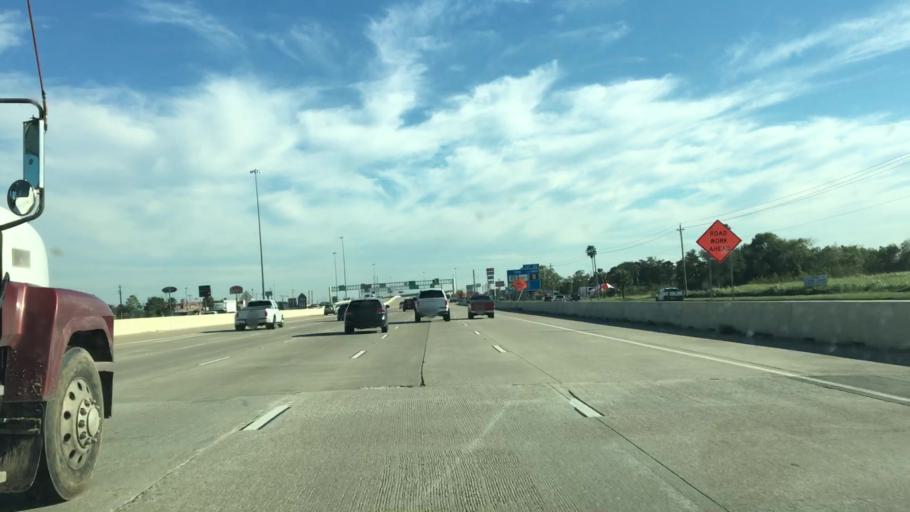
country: US
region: Texas
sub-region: Harris County
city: Webster
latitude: 29.5334
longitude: -95.1356
